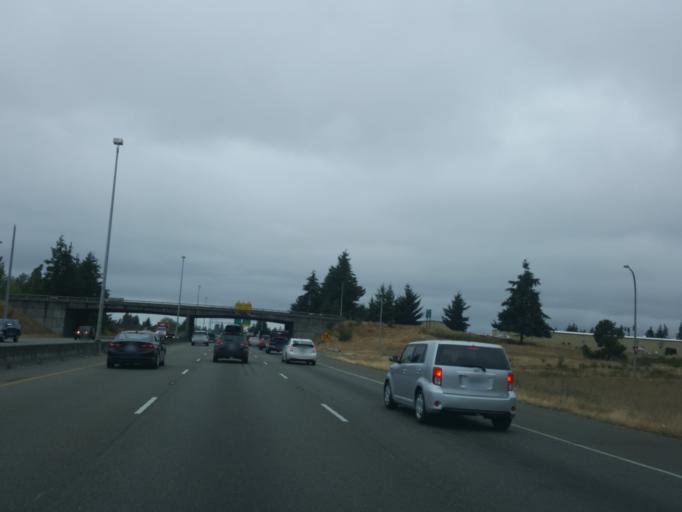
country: US
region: Washington
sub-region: Pierce County
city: Parkland
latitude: 47.1598
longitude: -122.4661
